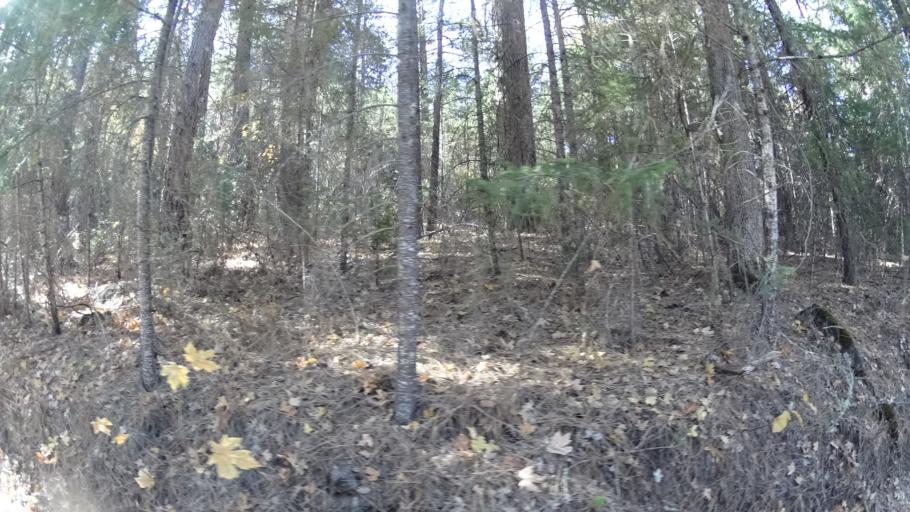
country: US
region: California
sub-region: Siskiyou County
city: Yreka
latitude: 41.8644
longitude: -122.7924
